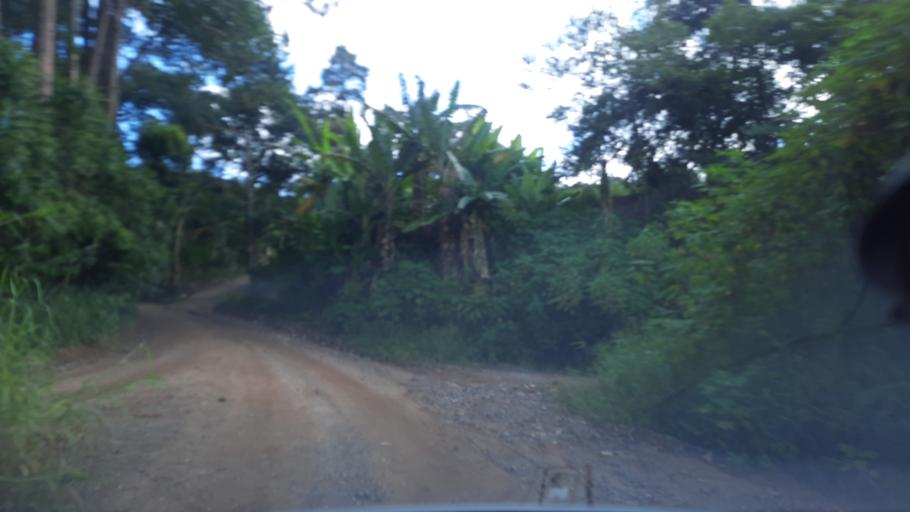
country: BR
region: Sao Paulo
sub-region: Atibaia
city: Atibaia
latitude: -23.0800
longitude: -46.5090
